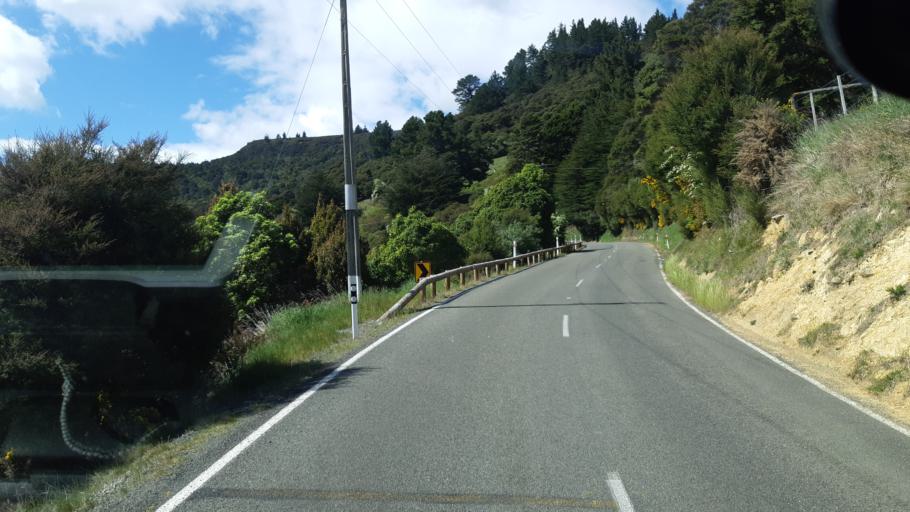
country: NZ
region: Otago
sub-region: Dunedin City
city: Portobello
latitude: -45.7775
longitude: 170.5927
